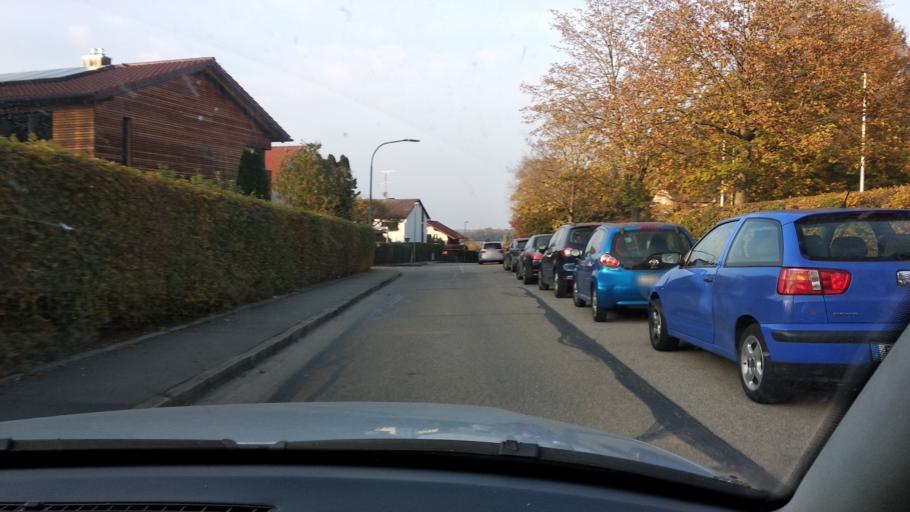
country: DE
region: Bavaria
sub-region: Upper Bavaria
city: Worth
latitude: 48.2431
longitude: 11.9018
